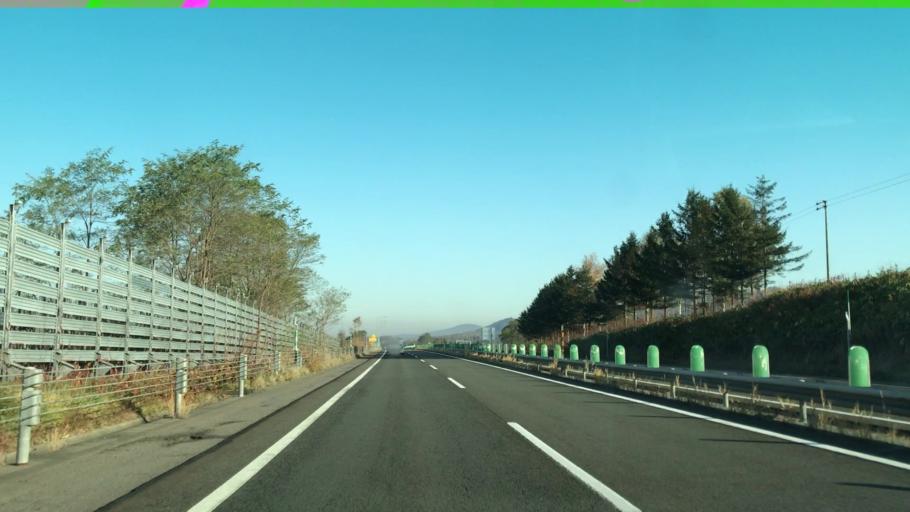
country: JP
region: Hokkaido
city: Sunagawa
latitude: 43.4350
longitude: 141.9153
